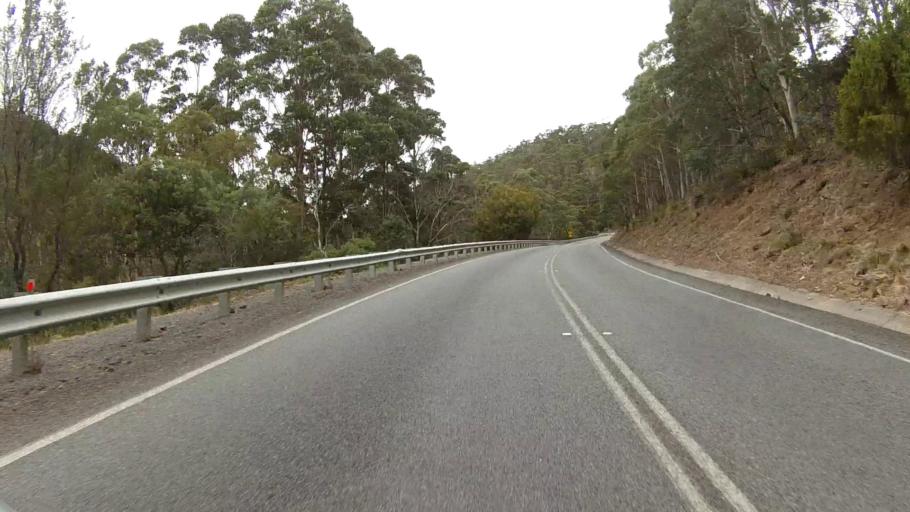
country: AU
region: Tasmania
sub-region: Sorell
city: Sorell
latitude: -42.6720
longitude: 147.5263
